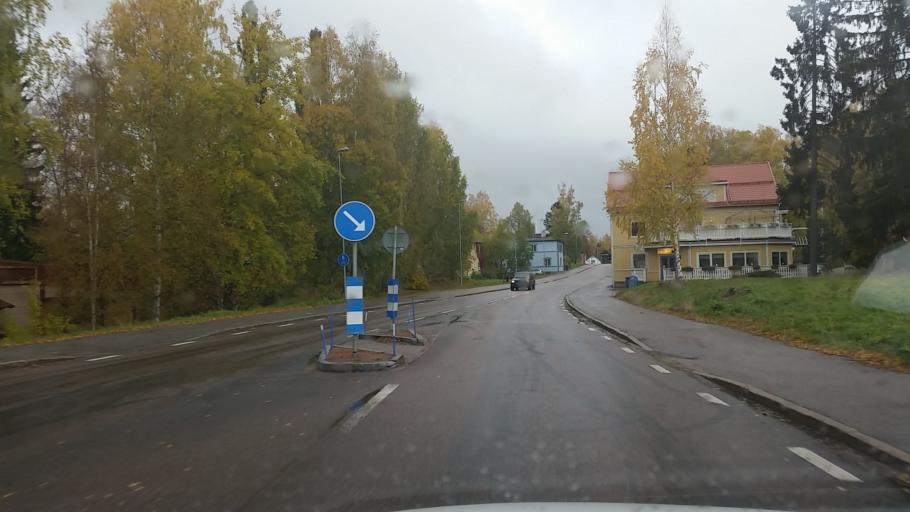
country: SE
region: Gaevleborg
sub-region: Sandvikens Kommun
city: Jarbo
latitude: 60.5854
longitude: 16.5303
